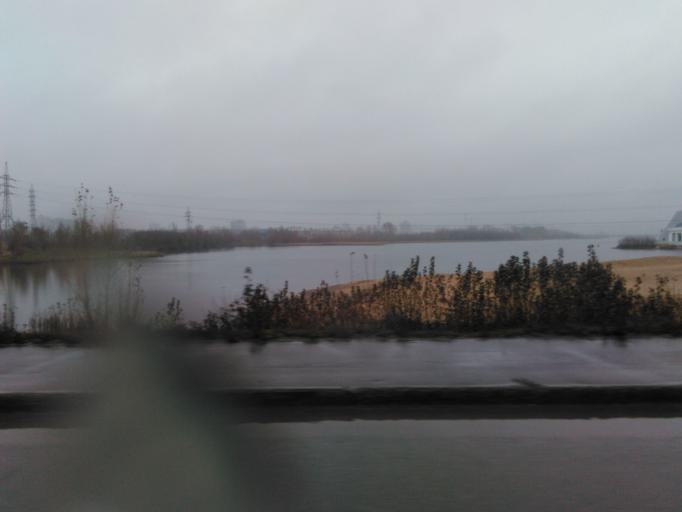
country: RU
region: Tatarstan
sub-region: Gorod Kazan'
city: Kazan
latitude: 55.7999
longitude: 49.0725
